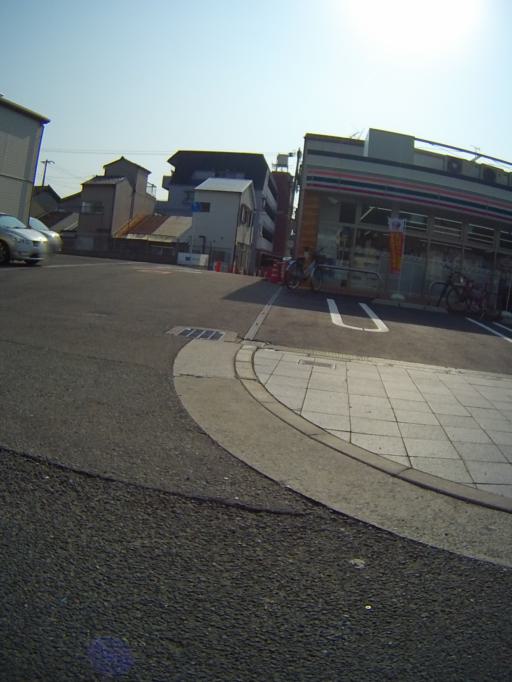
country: JP
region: Osaka
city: Osaka-shi
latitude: 34.6804
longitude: 135.4553
